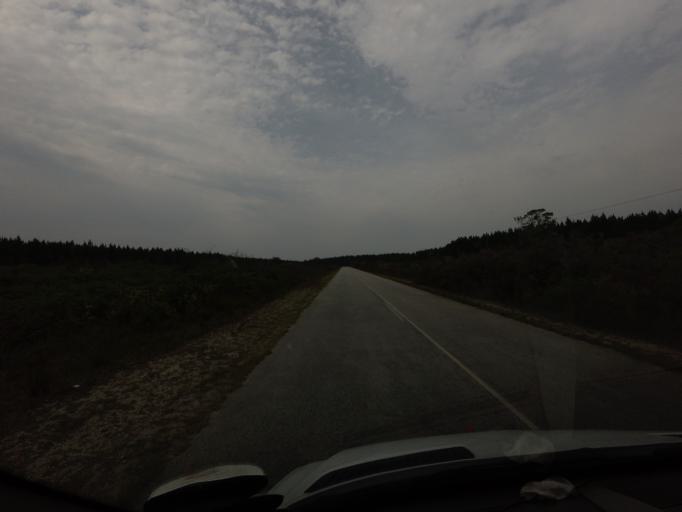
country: ZA
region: Eastern Cape
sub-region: Cacadu District Municipality
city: Kareedouw
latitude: -33.9857
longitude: 23.8429
